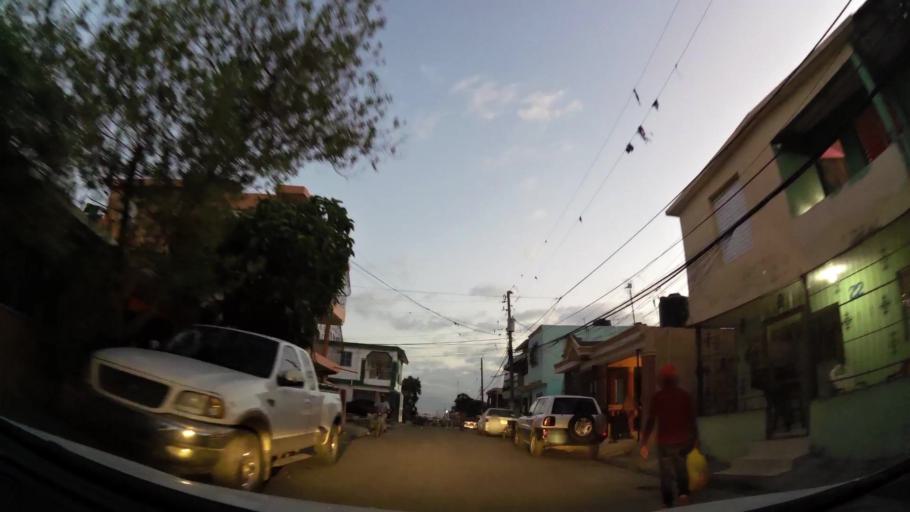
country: DO
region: Nacional
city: La Agustina
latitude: 18.5436
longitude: -69.9400
